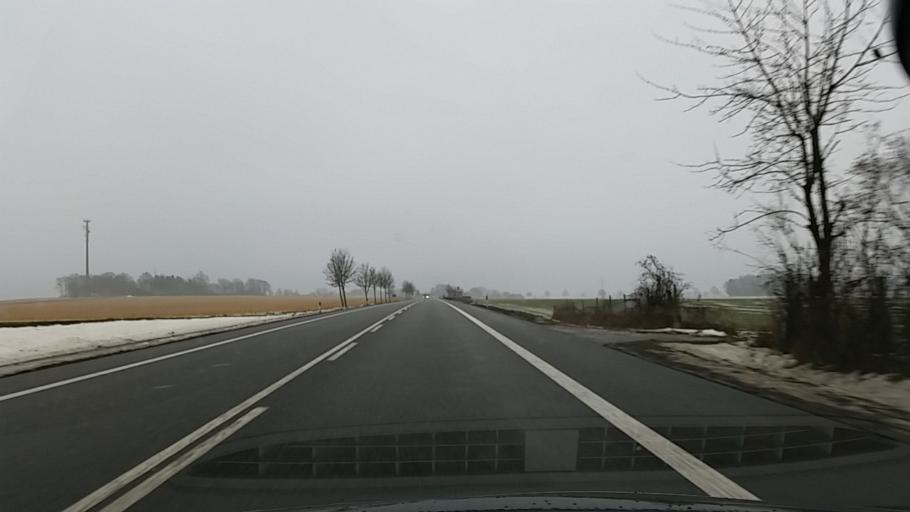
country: DE
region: Lower Saxony
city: Barum
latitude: 53.0568
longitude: 10.5346
